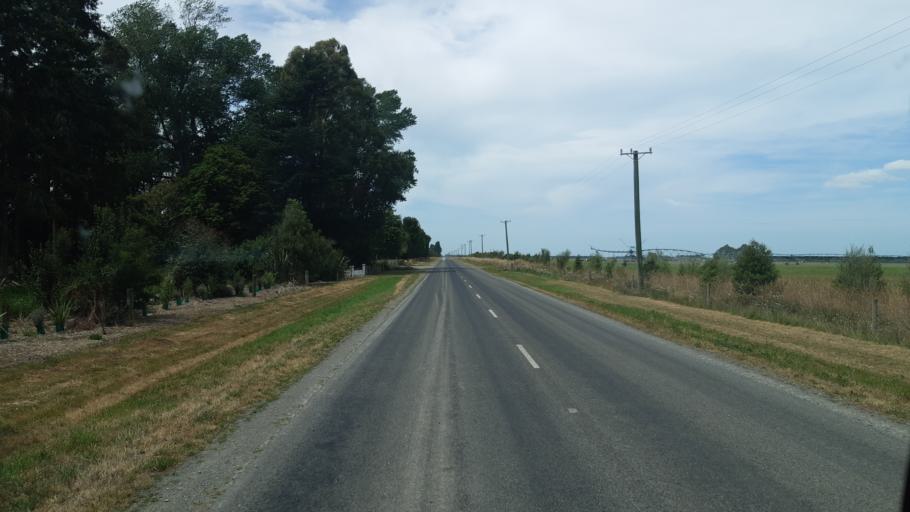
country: NZ
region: Canterbury
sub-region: Ashburton District
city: Tinwald
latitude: -43.9214
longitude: 171.5398
